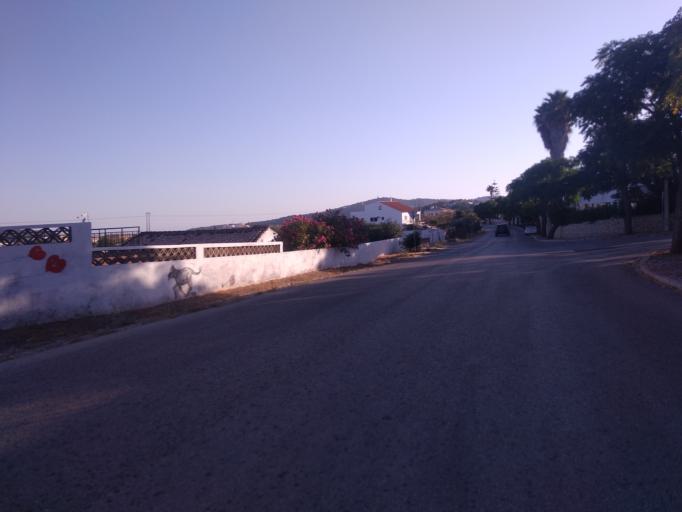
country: PT
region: Faro
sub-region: Sao Bras de Alportel
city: Sao Bras de Alportel
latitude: 37.1610
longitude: -7.8909
